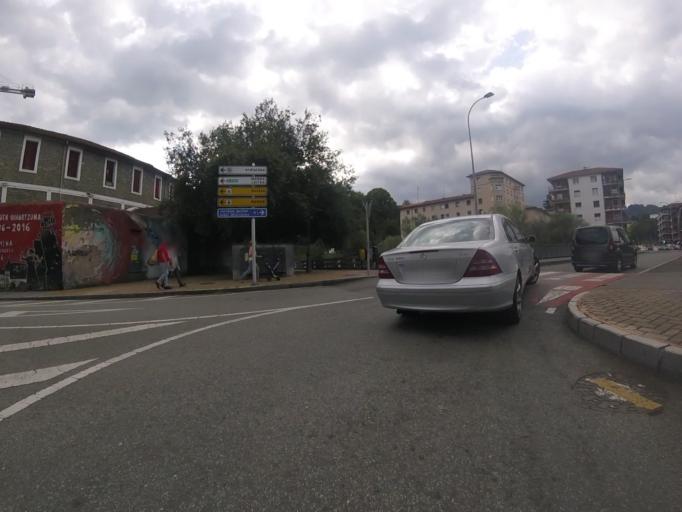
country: ES
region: Basque Country
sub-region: Provincia de Guipuzcoa
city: Tolosa
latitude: 43.1331
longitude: -2.0773
